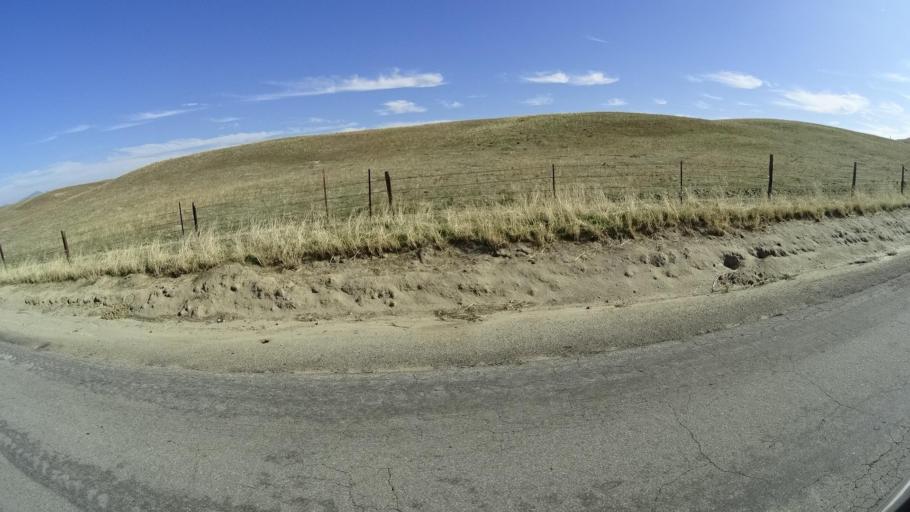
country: US
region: California
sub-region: Tulare County
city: Richgrove
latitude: 35.6399
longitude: -118.9431
